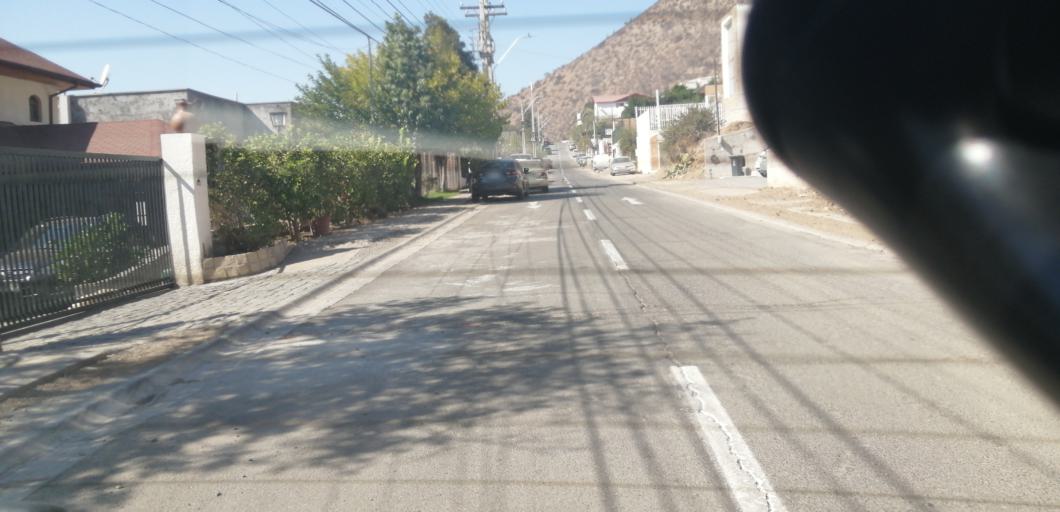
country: CL
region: Santiago Metropolitan
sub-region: Provincia de Santiago
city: Lo Prado
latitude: -33.4571
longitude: -70.8245
